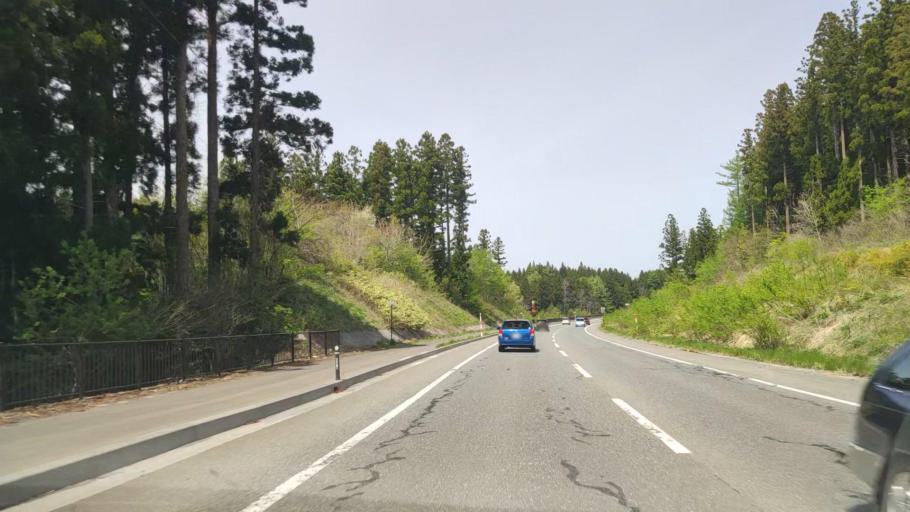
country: JP
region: Aomori
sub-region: Misawa Shi
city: Inuotose
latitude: 40.6884
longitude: 141.1691
